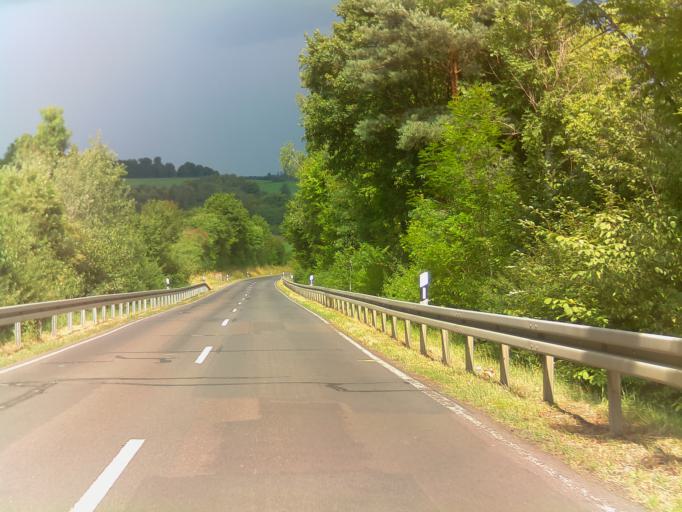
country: DE
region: Hesse
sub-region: Regierungsbezirk Kassel
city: Hosenfeld
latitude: 50.5529
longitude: 9.4320
